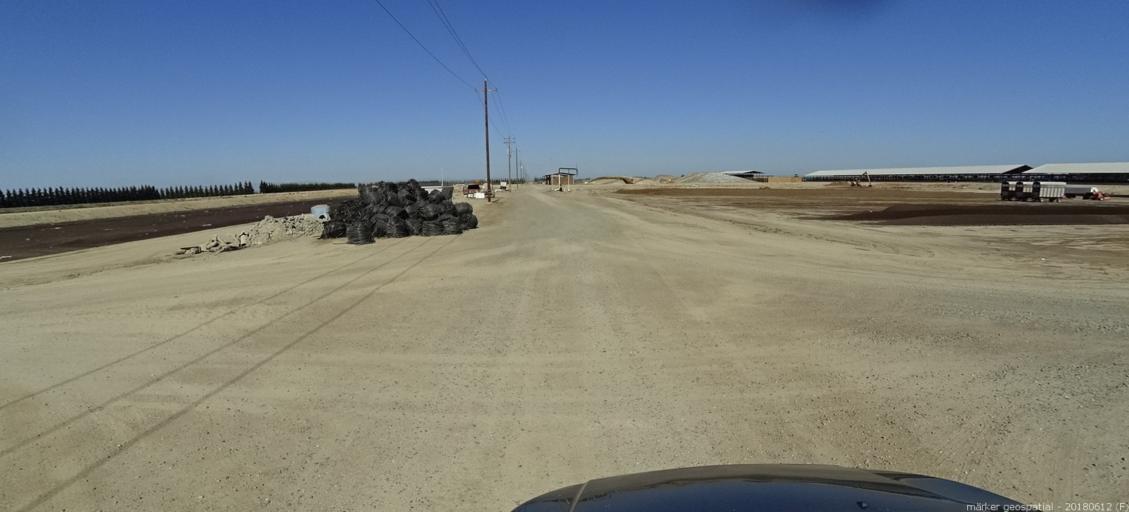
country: US
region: California
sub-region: Madera County
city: Chowchilla
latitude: 37.0108
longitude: -120.3700
